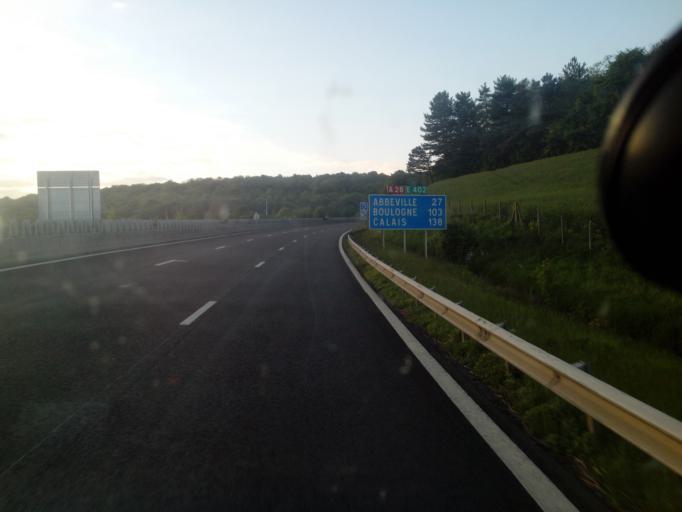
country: FR
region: Picardie
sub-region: Departement de la Somme
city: Bouttencourt
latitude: 49.9380
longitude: 1.6399
